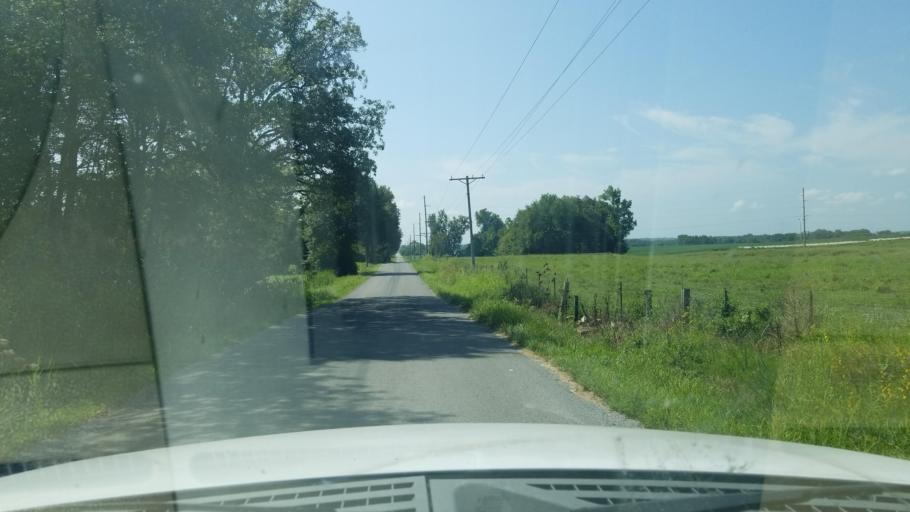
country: US
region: Illinois
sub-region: Saline County
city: Harrisburg
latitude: 37.8511
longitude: -88.6517
